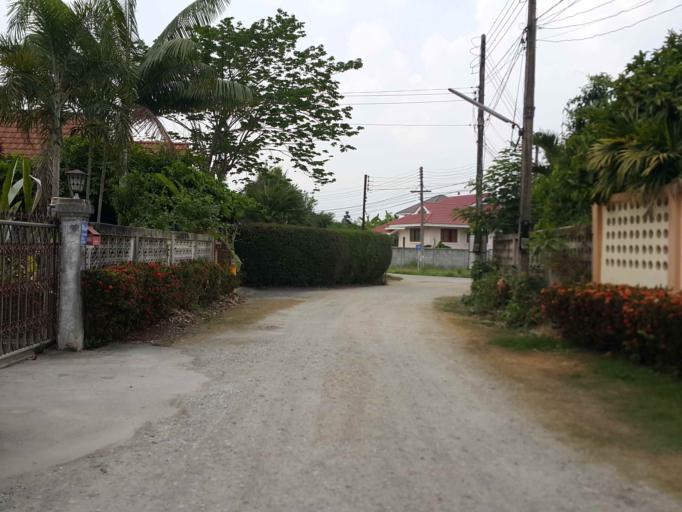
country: TH
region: Chiang Mai
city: Saraphi
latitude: 18.7497
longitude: 99.0191
